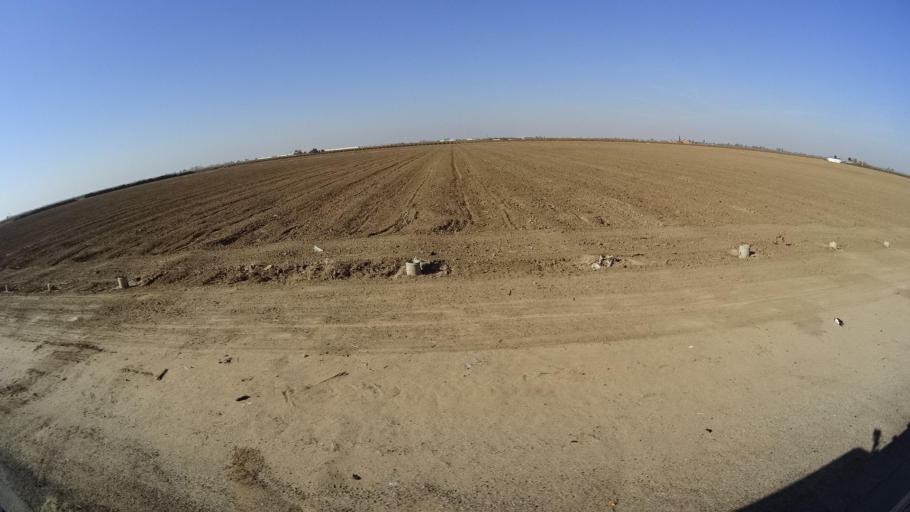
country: US
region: California
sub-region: Kern County
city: Delano
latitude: 35.7347
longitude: -119.2052
